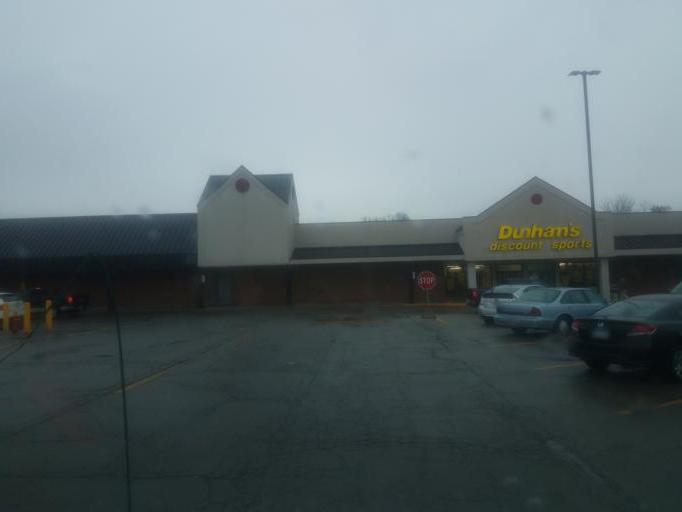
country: US
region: Ohio
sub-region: Marion County
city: Marion
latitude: 40.5820
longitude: -83.0957
